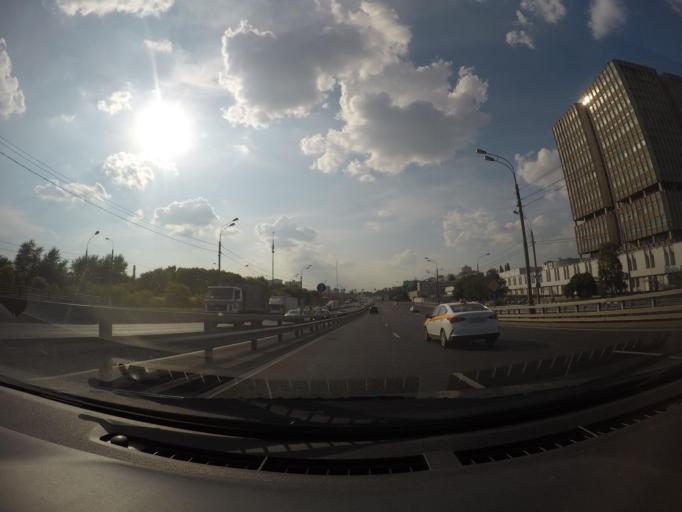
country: RU
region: Moscow
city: Veshnyaki
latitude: 55.7127
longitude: 37.8321
